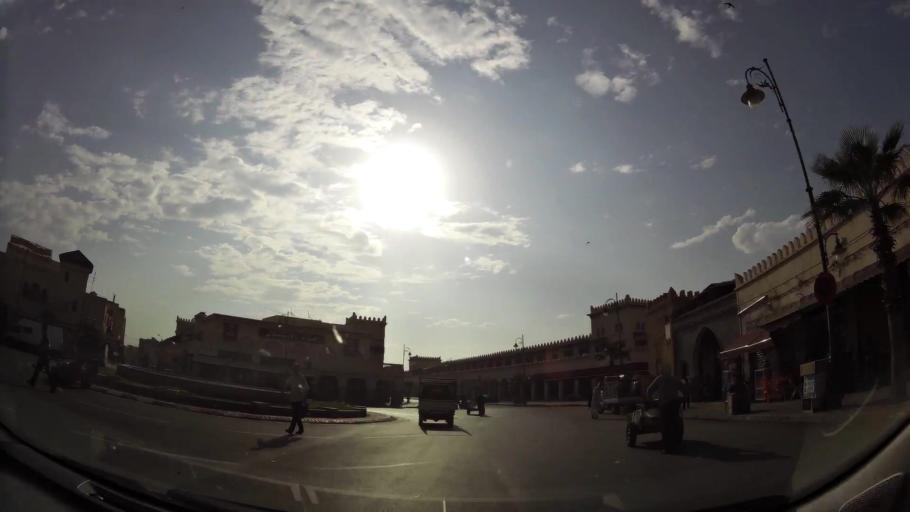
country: MA
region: Oriental
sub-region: Oujda-Angad
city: Oujda
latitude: 34.6816
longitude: -1.9110
